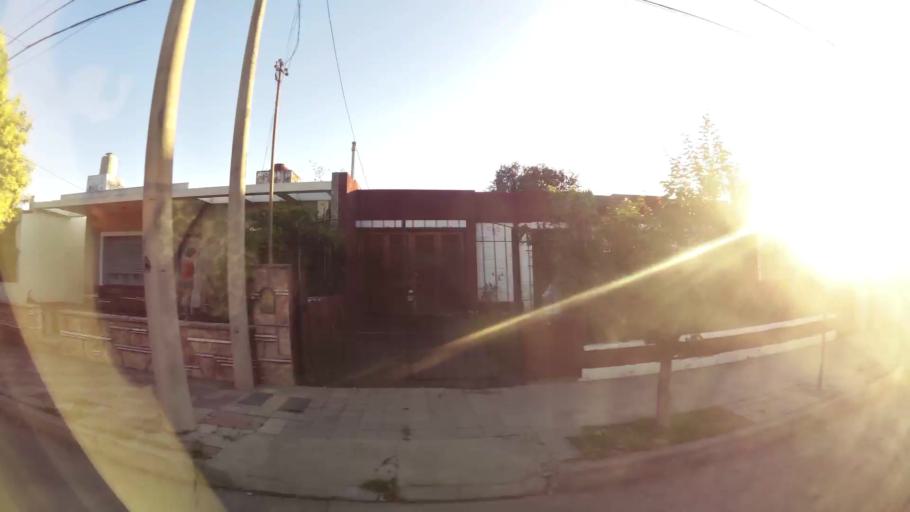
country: AR
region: Cordoba
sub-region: Departamento de Capital
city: Cordoba
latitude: -31.3892
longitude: -64.2125
